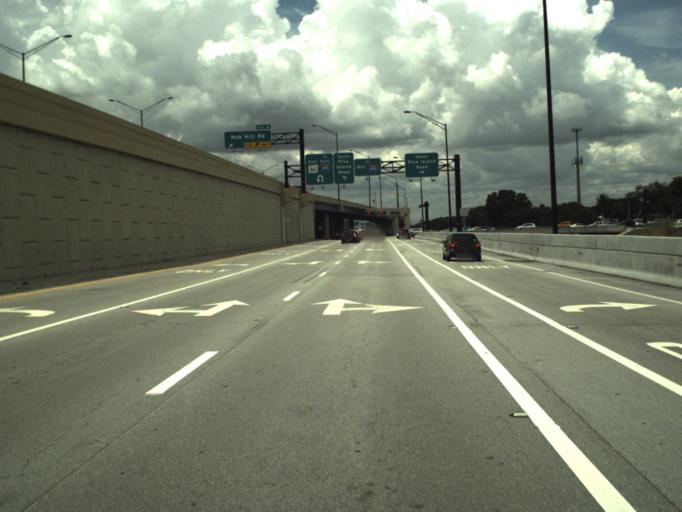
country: US
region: Florida
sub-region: Broward County
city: Pine Island Ridge
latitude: 26.1027
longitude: -80.2632
